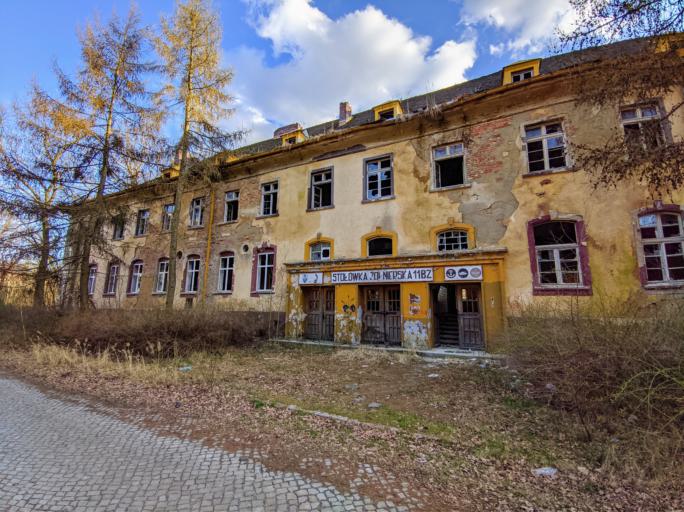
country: PL
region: Lubusz
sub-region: Powiat zarski
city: Zary
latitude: 51.6374
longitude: 15.1744
